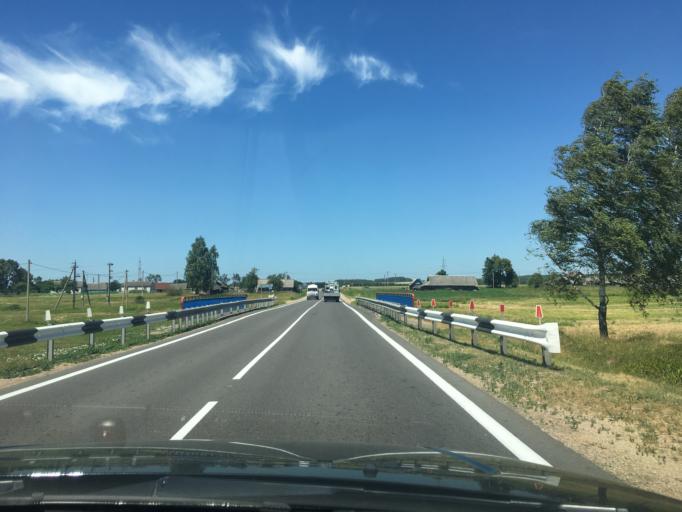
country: BY
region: Grodnenskaya
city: Hal'shany
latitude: 54.0995
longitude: 25.9156
